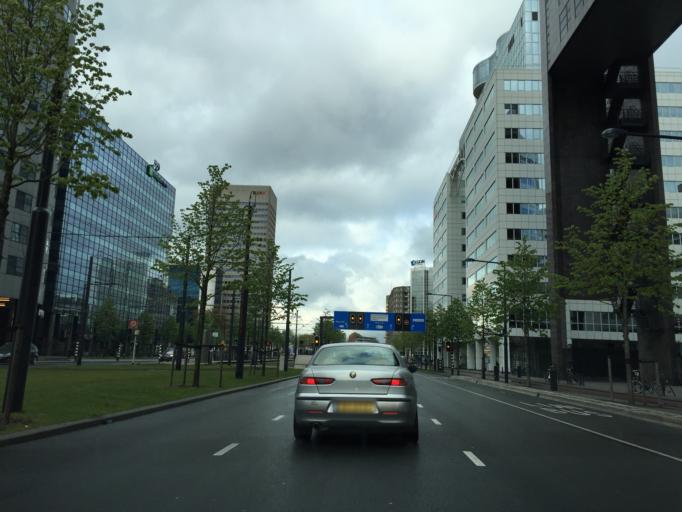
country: NL
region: South Holland
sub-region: Gemeente Rotterdam
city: Rotterdam
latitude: 51.9236
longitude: 4.4744
